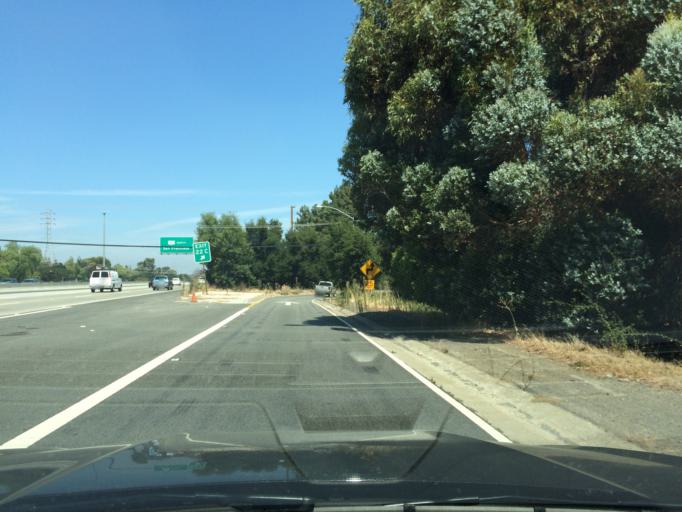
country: US
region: California
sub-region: Santa Clara County
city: Mountain View
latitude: 37.3818
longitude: -122.0679
